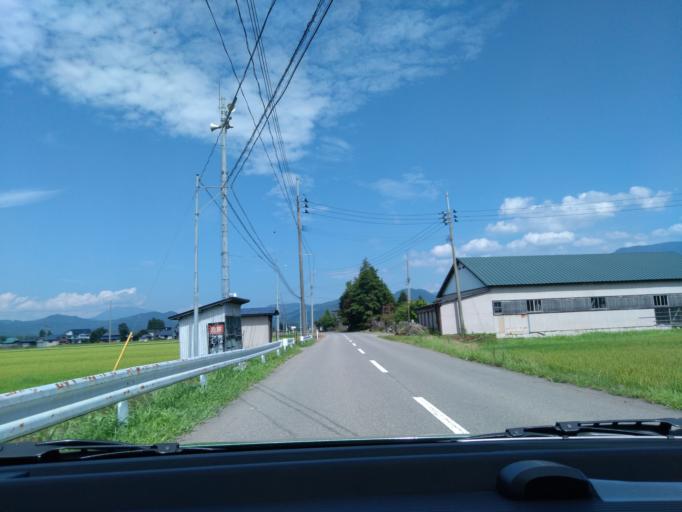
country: JP
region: Akita
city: Kakunodatemachi
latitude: 39.6027
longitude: 140.5859
